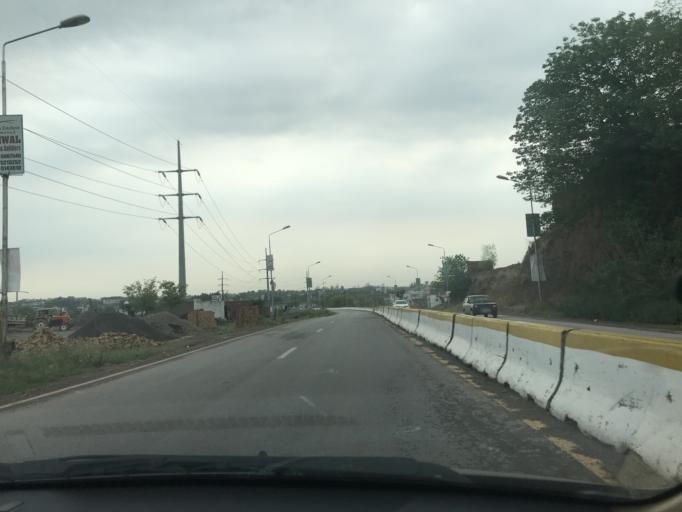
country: PK
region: Islamabad
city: Islamabad
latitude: 33.6921
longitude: 73.1733
